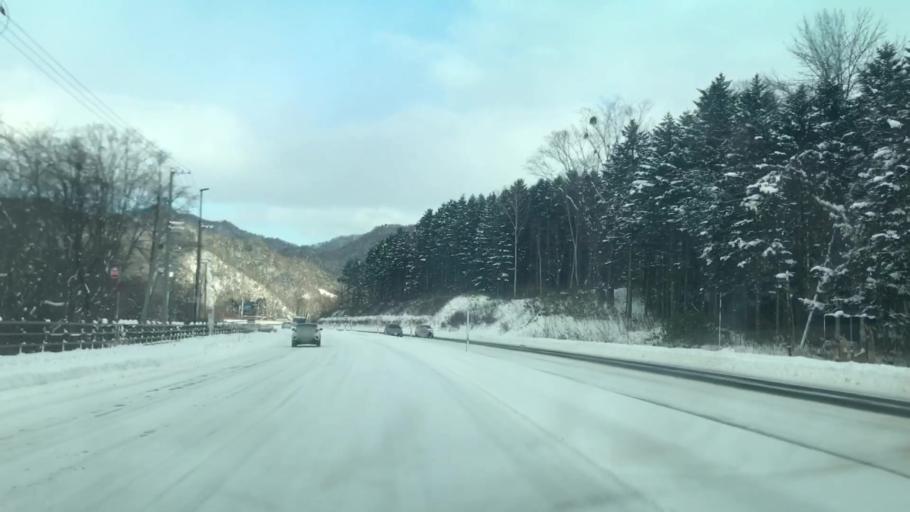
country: JP
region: Hokkaido
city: Sapporo
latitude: 42.9685
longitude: 141.2037
